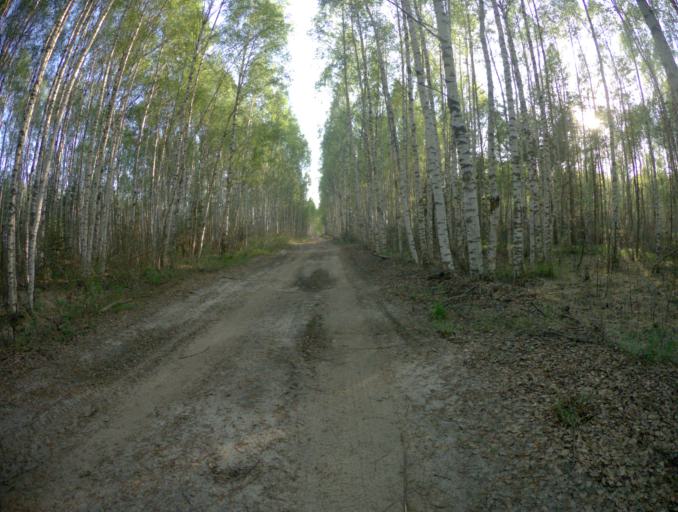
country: RU
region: Vladimir
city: Vyazniki
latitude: 56.3728
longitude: 42.1664
